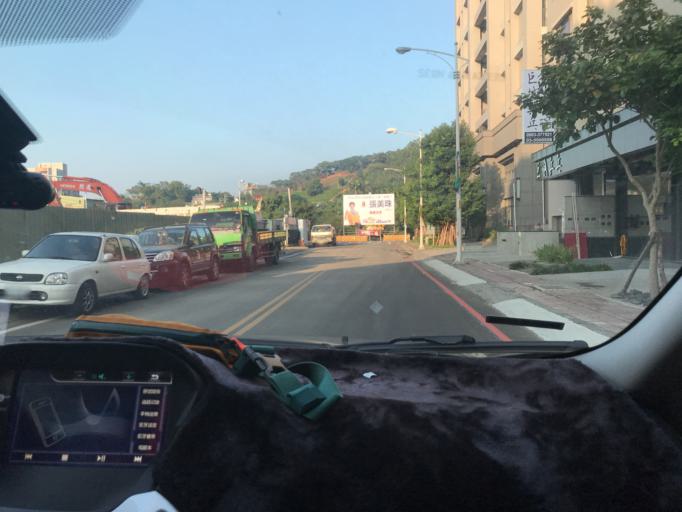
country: TW
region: Taiwan
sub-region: Hsinchu
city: Zhubei
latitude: 24.8248
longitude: 121.0346
